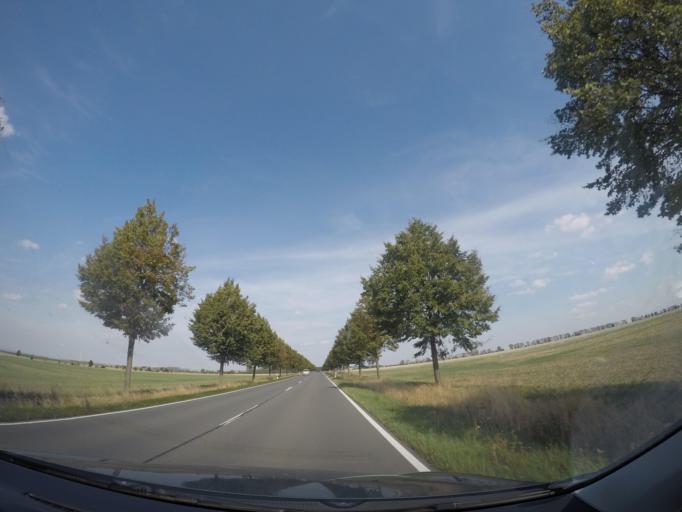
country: DE
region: Saxony-Anhalt
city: Langeln
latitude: 51.9023
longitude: 10.7771
